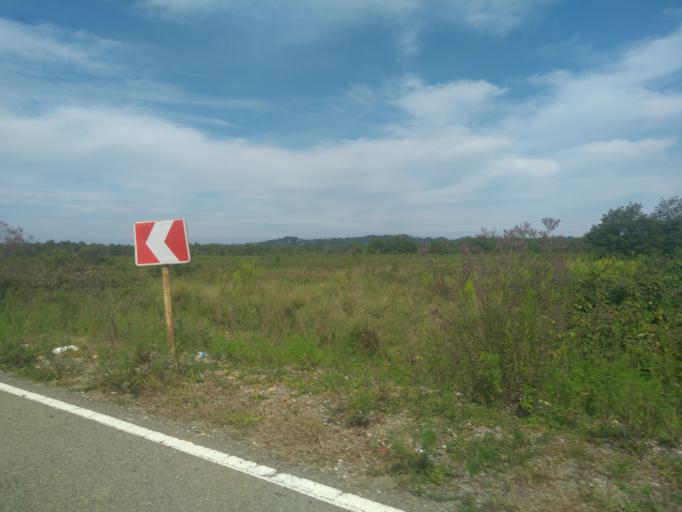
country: GE
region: Guria
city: Urek'i
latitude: 41.9207
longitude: 41.7774
